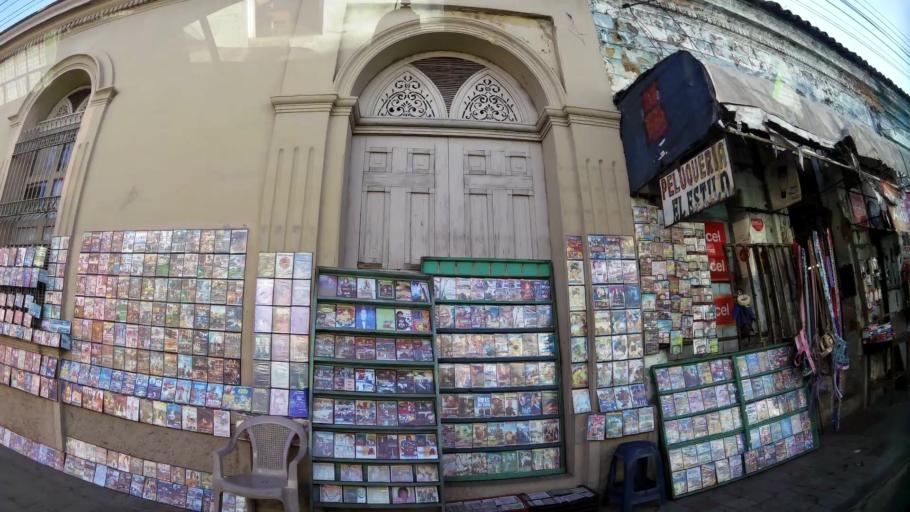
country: SV
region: Santa Ana
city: Santa Ana
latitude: 13.9912
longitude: -89.5619
